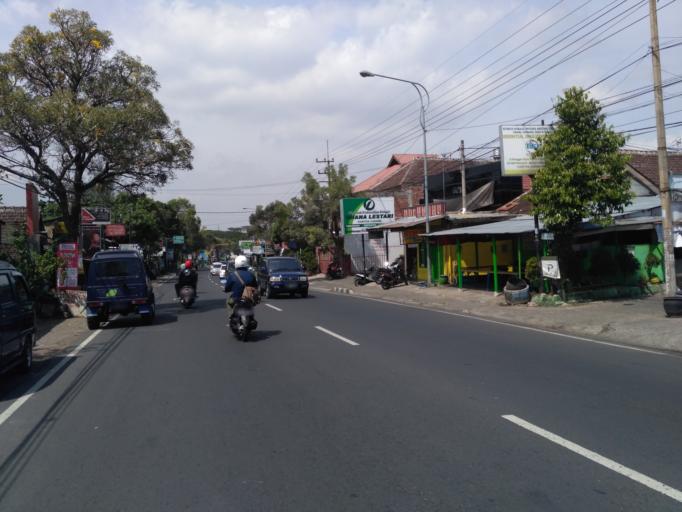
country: ID
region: East Java
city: Batu
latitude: -7.9121
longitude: 112.5834
